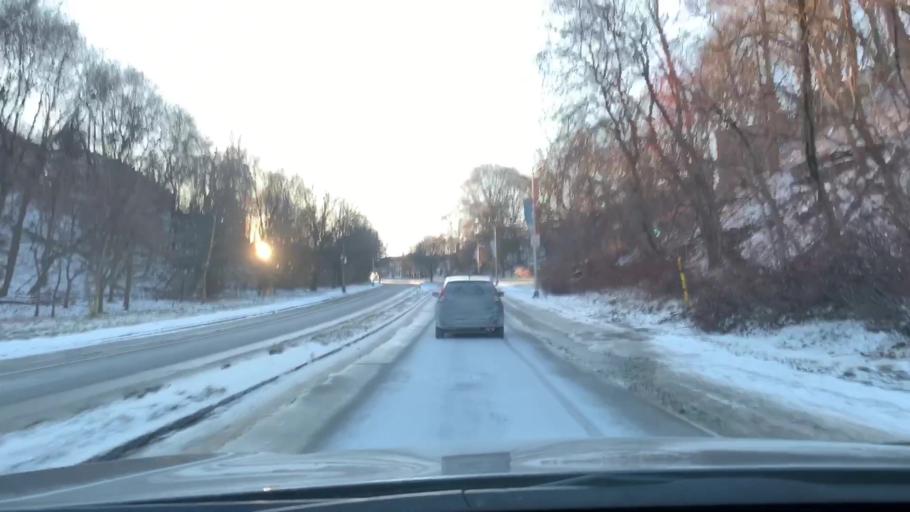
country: US
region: Pennsylvania
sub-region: Allegheny County
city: Aspinwall
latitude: 40.4670
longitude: -79.9160
